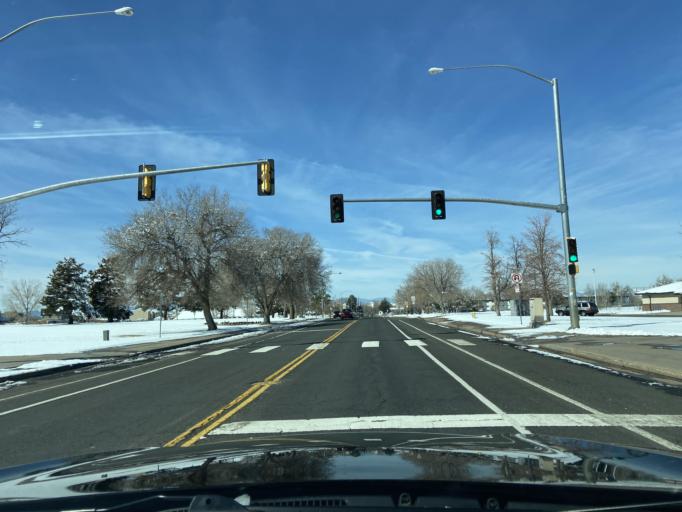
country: US
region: Colorado
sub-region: Adams County
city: Aurora
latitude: 39.7039
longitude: -104.8588
